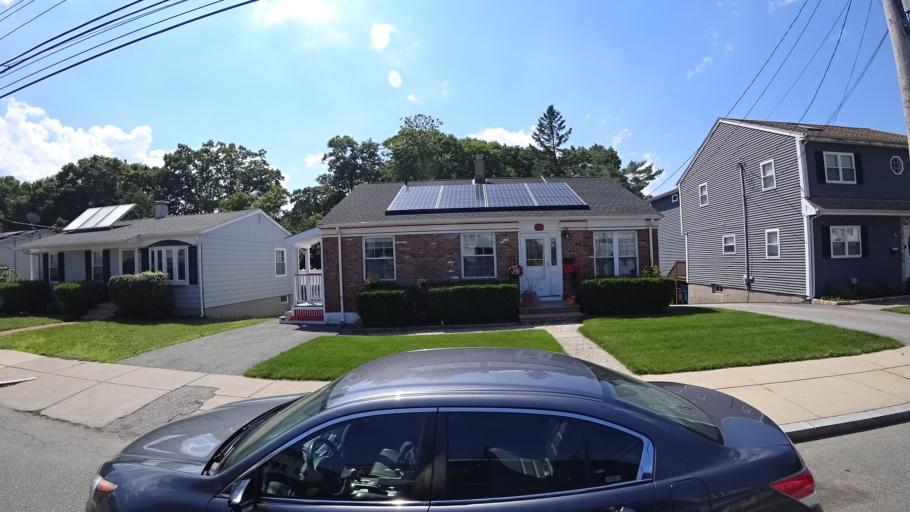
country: US
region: Massachusetts
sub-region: Norfolk County
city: Dedham
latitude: 42.2707
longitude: -71.1670
